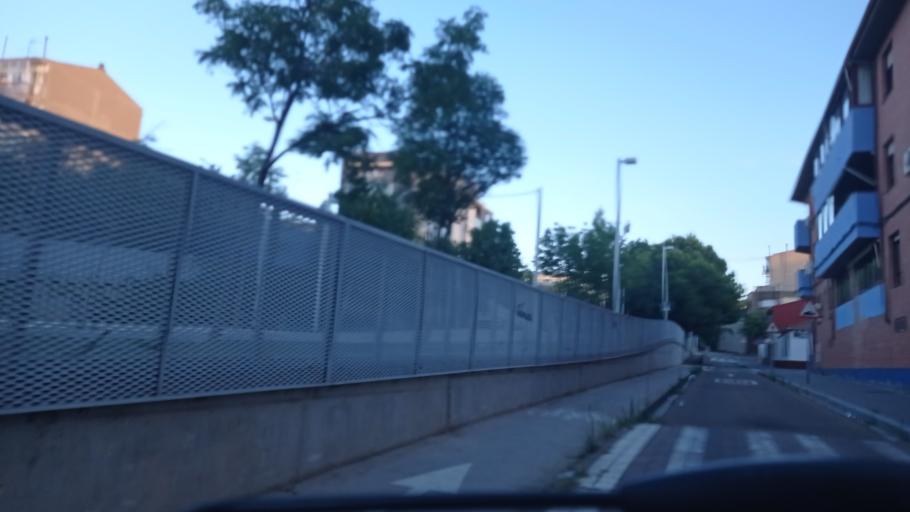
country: ES
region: Aragon
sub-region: Provincia de Zaragoza
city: Oliver-Valdefierro, Oliver, Valdefierro
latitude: 41.6541
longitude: -0.9247
